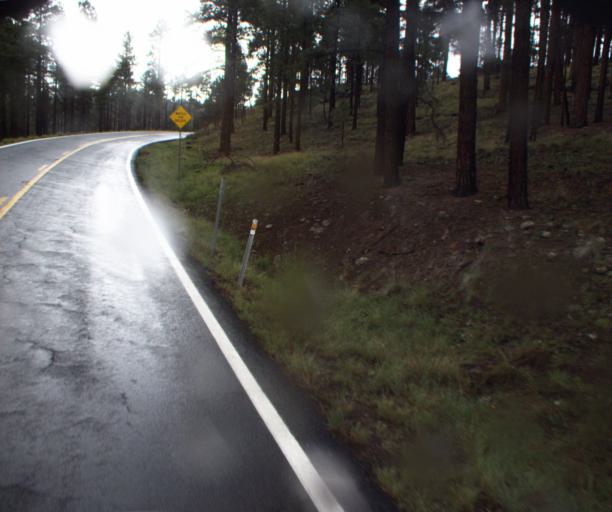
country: US
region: Arizona
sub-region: Apache County
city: Eagar
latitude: 33.7562
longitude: -109.2169
